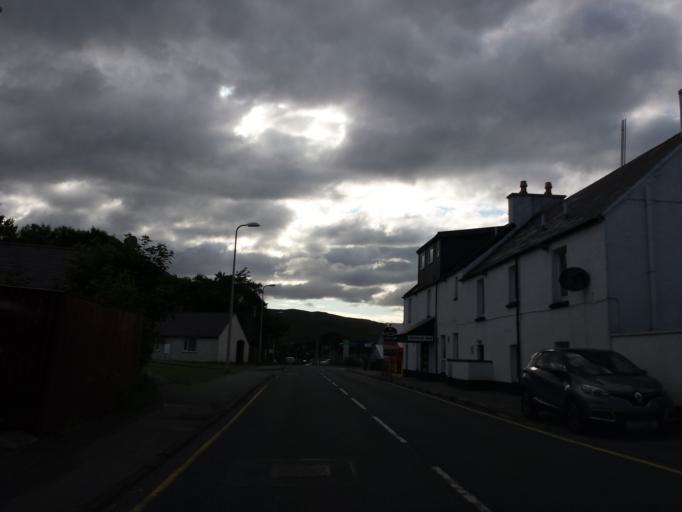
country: GB
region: Scotland
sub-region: Highland
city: Portree
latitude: 57.2409
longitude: -5.9052
